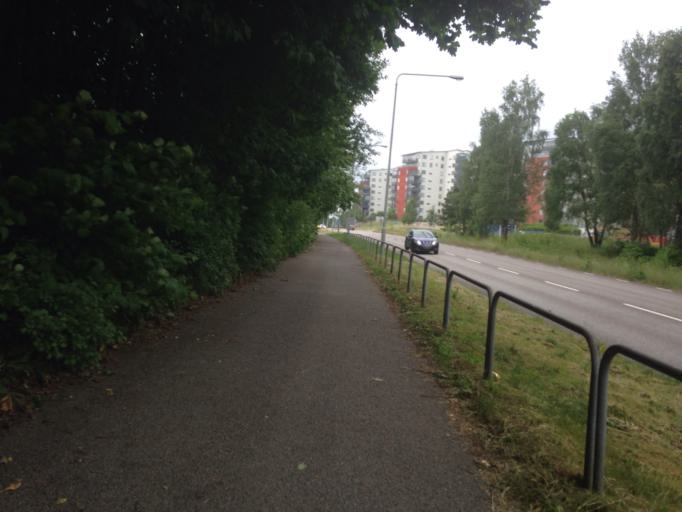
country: SE
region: Vaestra Goetaland
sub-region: Partille Kommun
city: Partille
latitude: 57.7200
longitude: 12.0612
